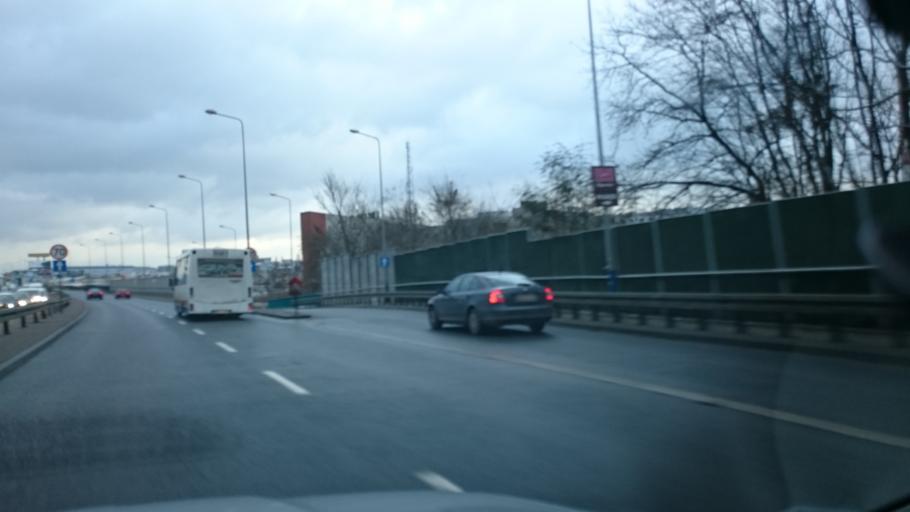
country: PL
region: Lesser Poland Voivodeship
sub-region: Krakow
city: Krakow
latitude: 50.0301
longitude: 19.9516
